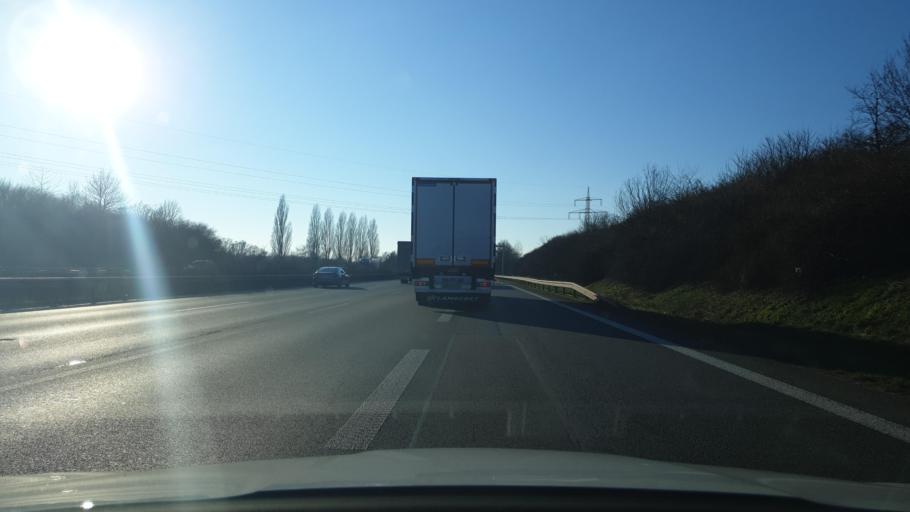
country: DE
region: North Rhine-Westphalia
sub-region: Regierungsbezirk Detmold
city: Vlotho
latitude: 52.2107
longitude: 8.8693
